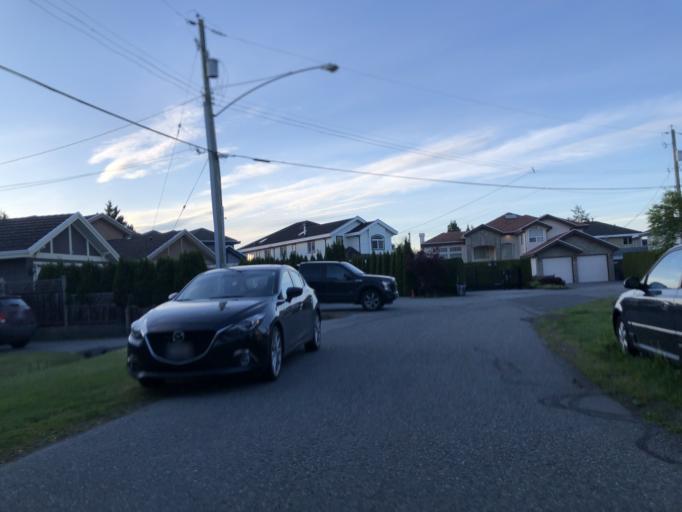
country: CA
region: British Columbia
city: Richmond
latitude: 49.1395
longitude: -123.1322
